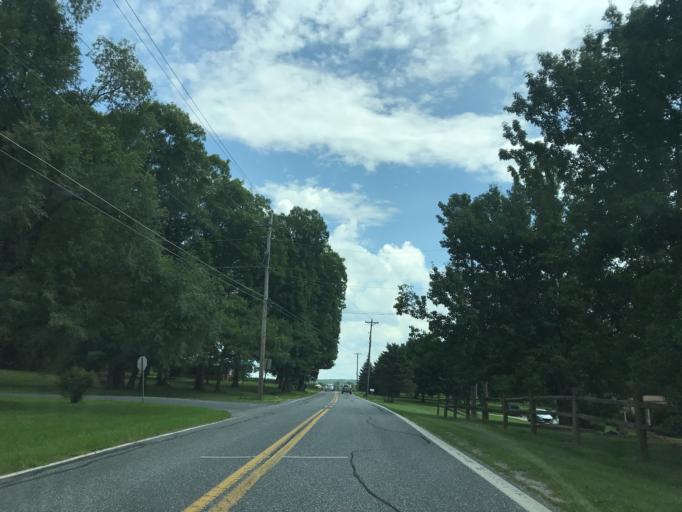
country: US
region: Pennsylvania
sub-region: York County
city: Dallastown
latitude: 39.8404
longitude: -76.6289
